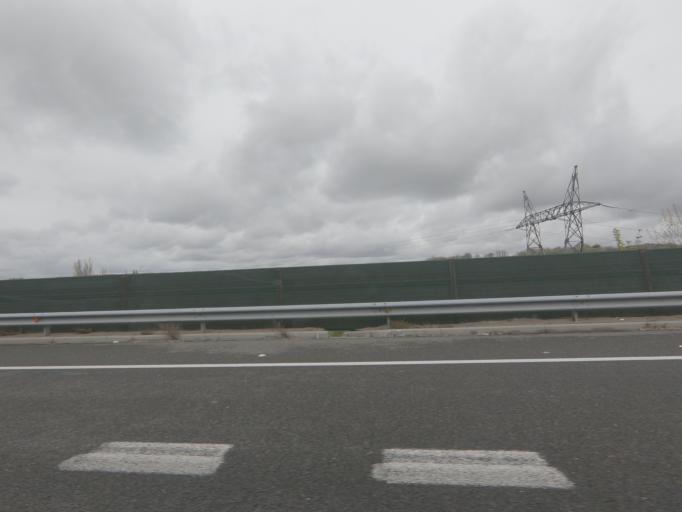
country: ES
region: Castille and Leon
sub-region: Provincia de Salamanca
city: Cantagallo
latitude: 40.3833
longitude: -5.8080
